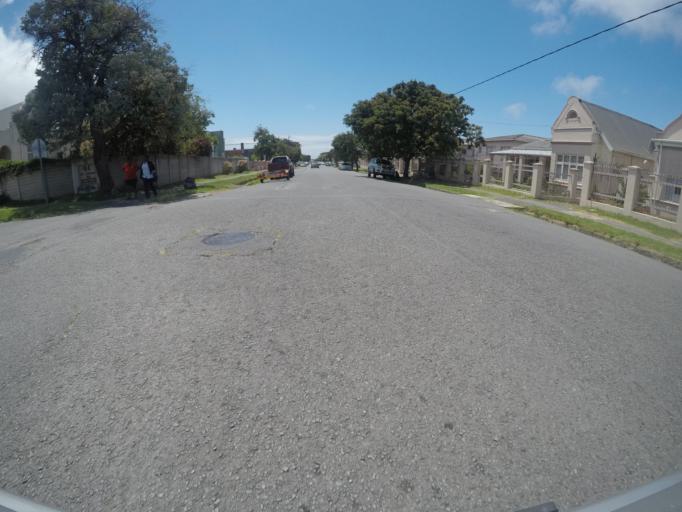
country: ZA
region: Eastern Cape
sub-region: Buffalo City Metropolitan Municipality
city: East London
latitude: -33.0005
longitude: 27.9023
